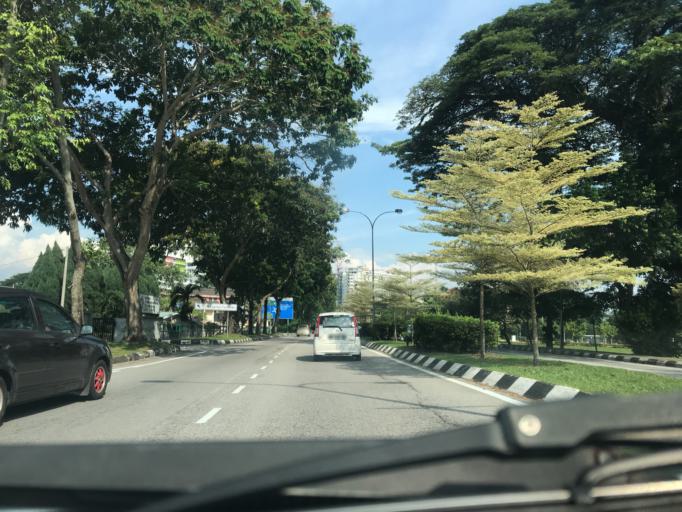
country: MY
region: Perak
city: Ipoh
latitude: 4.6063
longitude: 101.0853
